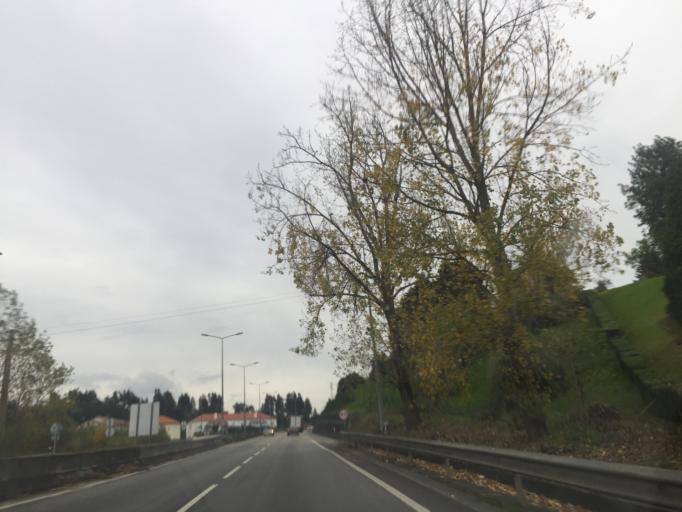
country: PT
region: Coimbra
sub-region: Coimbra
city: Coimbra
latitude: 40.1907
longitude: -8.4307
